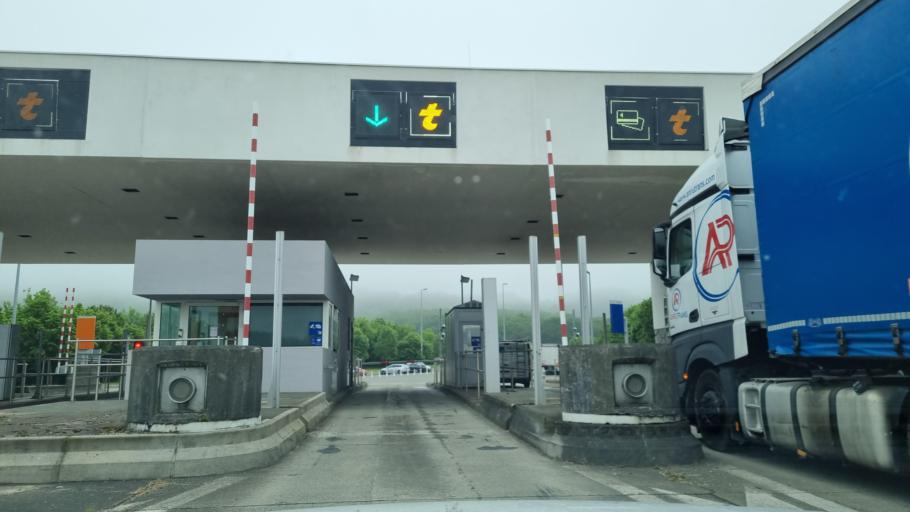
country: FR
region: Aquitaine
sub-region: Departement des Pyrenees-Atlantiques
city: Orthez
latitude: 43.4674
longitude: -0.7486
